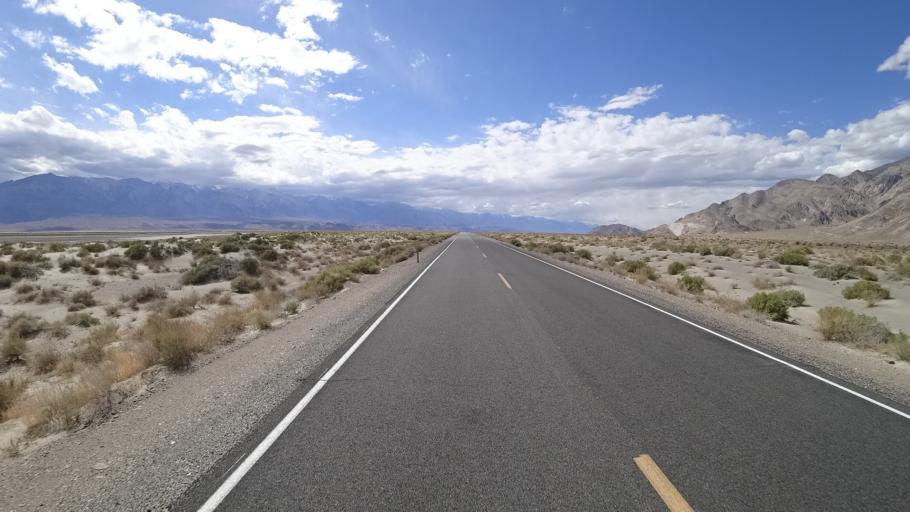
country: US
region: California
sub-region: Inyo County
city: Lone Pine
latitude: 36.5454
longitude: -117.9404
